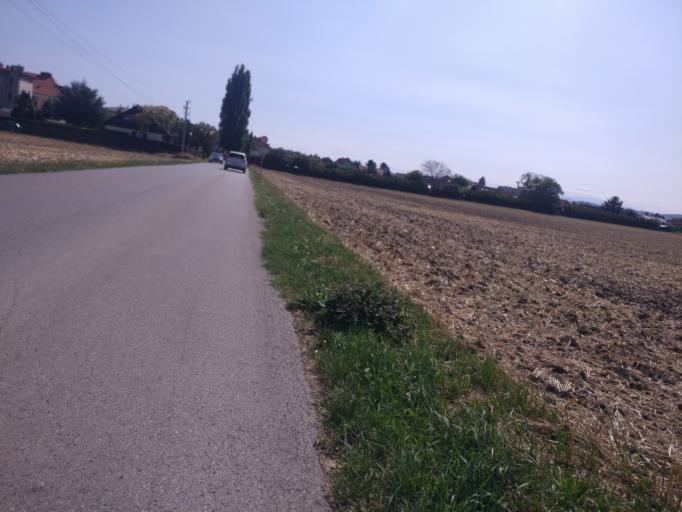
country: AT
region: Lower Austria
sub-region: Politischer Bezirk Modling
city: Guntramsdorf
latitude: 48.0313
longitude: 16.3070
